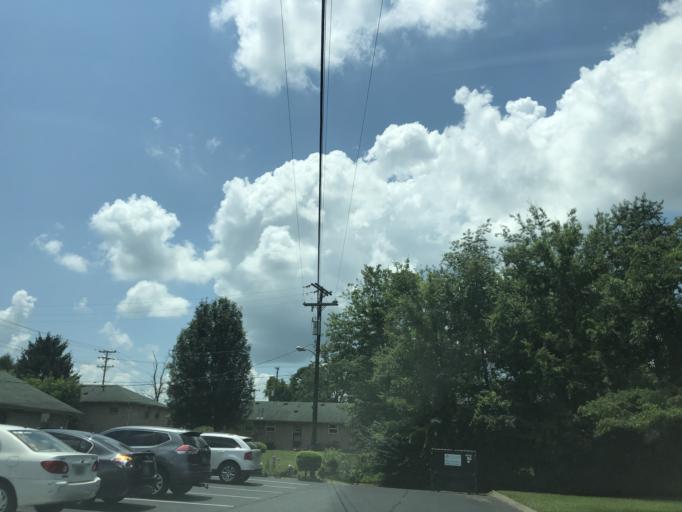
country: US
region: Tennessee
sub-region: Davidson County
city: Lakewood
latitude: 36.2031
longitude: -86.6171
